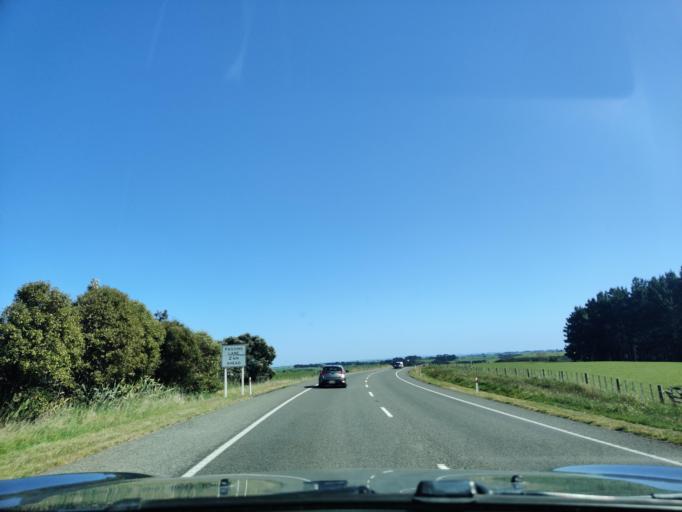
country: NZ
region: Manawatu-Wanganui
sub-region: Rangitikei District
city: Bulls
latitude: -40.0764
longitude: 175.2362
